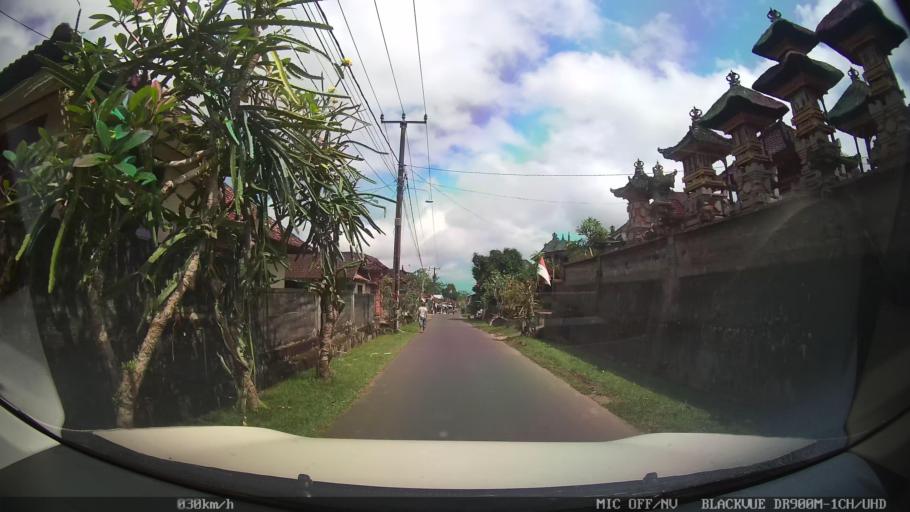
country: ID
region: Bali
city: Banjar Susut Kaja
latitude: -8.4419
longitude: 115.3298
